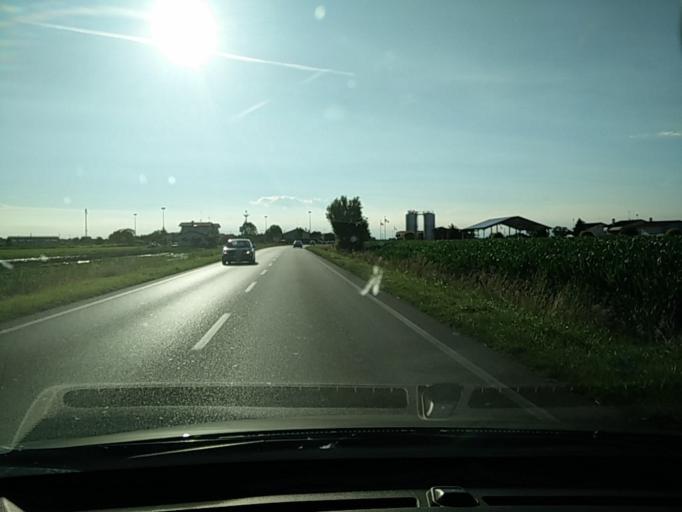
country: IT
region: Veneto
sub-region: Provincia di Venezia
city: Crepaldo
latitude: 45.5773
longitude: 12.6926
